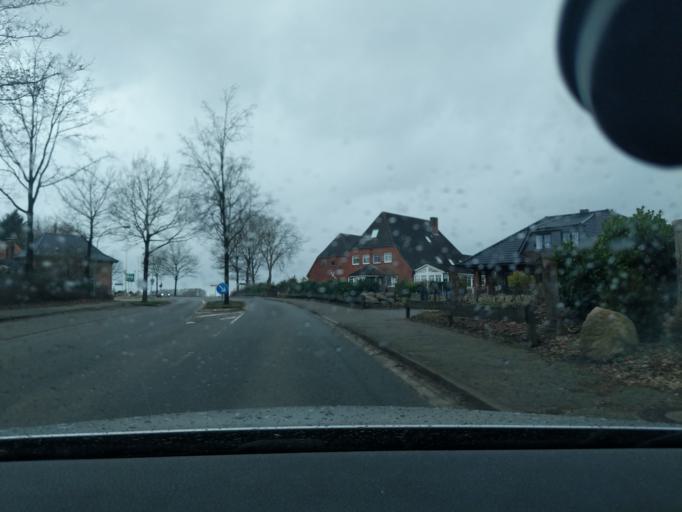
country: DE
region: Lower Saxony
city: Bargstedt
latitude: 53.4607
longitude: 9.4477
